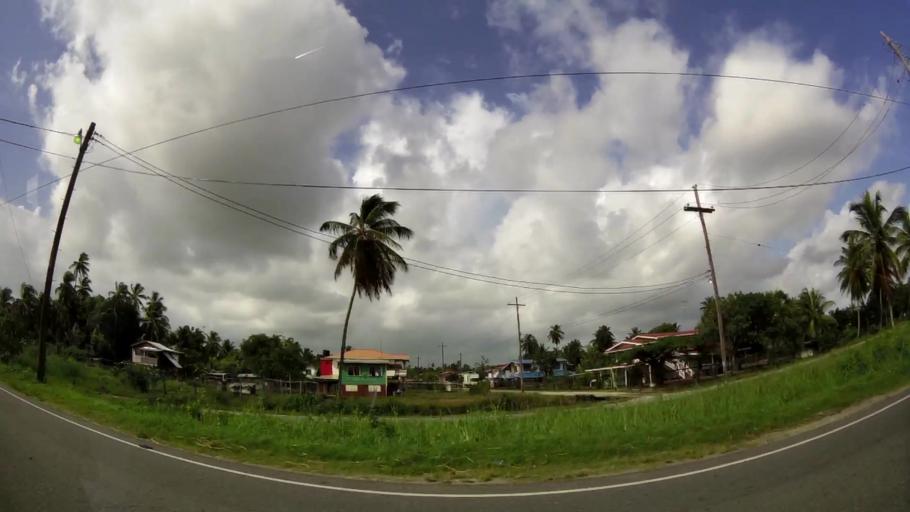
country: GY
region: Demerara-Mahaica
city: Mahaica Village
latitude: 6.6776
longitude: -57.9224
